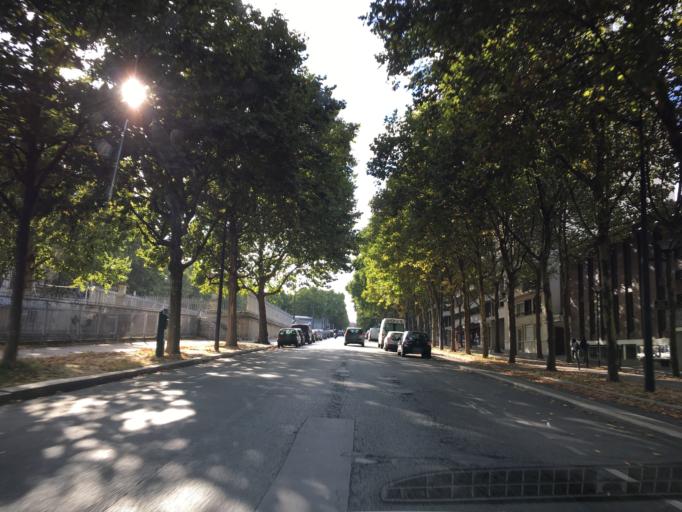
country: FR
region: Ile-de-France
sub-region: Departement du Val-de-Marne
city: Gentilly
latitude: 48.8327
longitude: 2.3386
